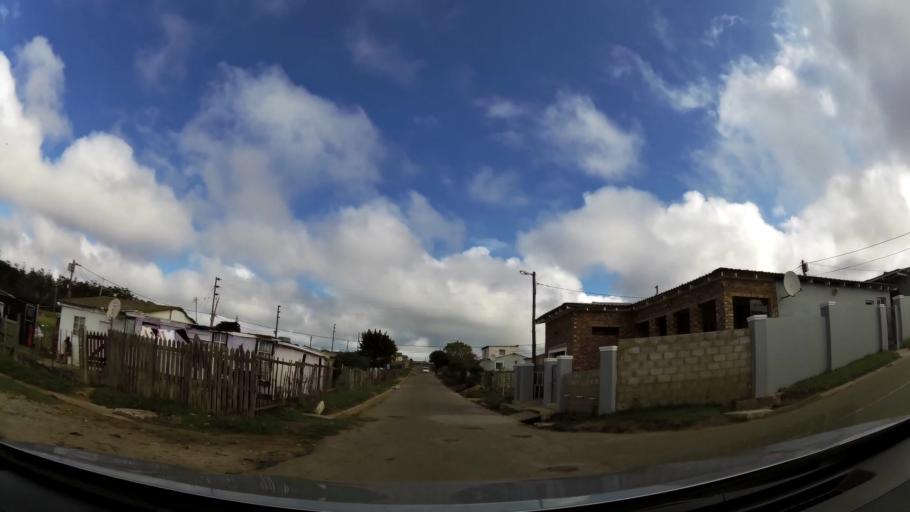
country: ZA
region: Western Cape
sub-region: Eden District Municipality
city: Plettenberg Bay
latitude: -34.0508
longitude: 23.3240
